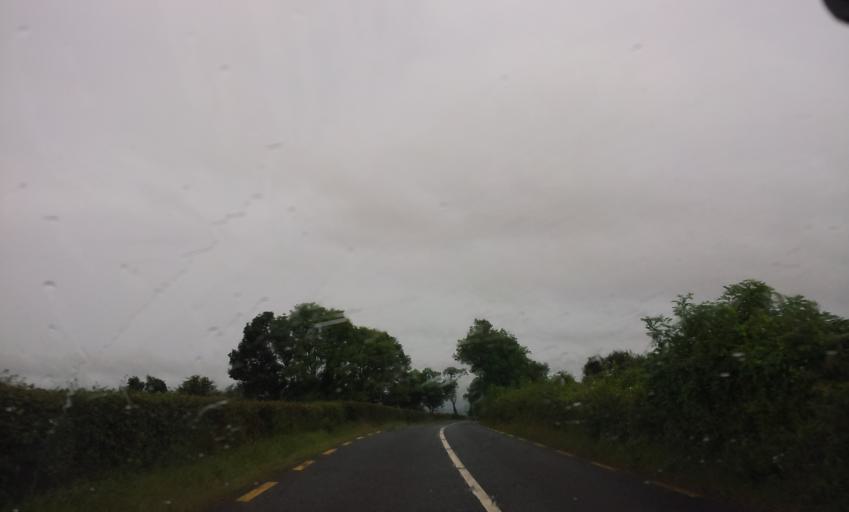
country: IE
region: Munster
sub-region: County Cork
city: Mallow
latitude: 52.2026
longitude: -8.5116
